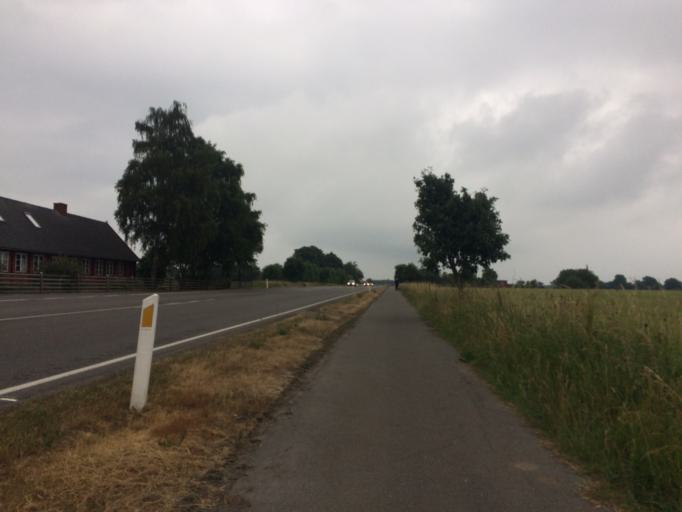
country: DK
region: Capital Region
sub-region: Bornholm Kommune
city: Ronne
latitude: 55.1094
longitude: 14.7480
